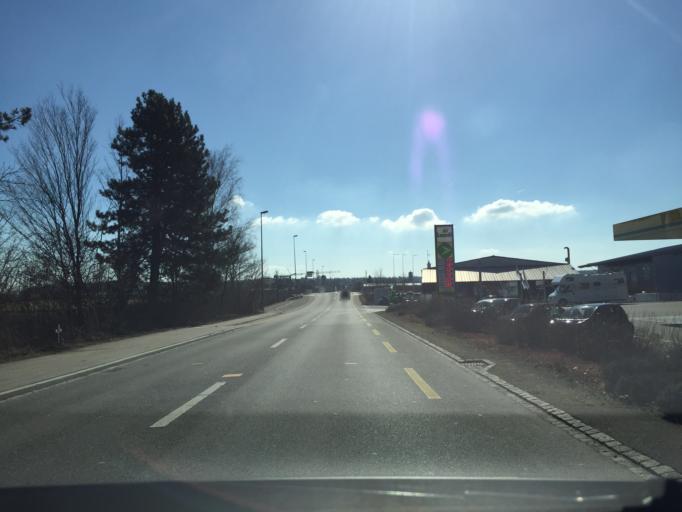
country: CH
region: Thurgau
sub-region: Frauenfeld District
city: Diessenhofen
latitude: 47.6814
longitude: 8.7502
